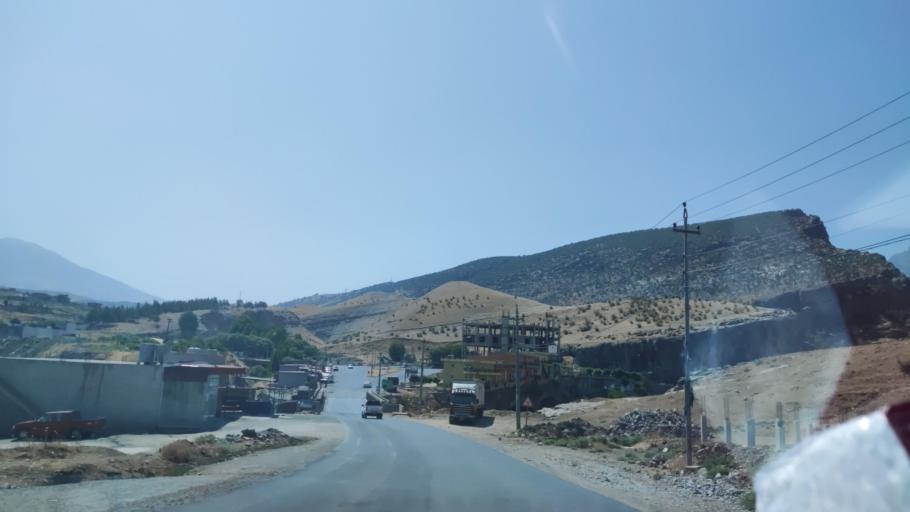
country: IQ
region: Arbil
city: Ruwandiz
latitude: 36.6504
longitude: 44.4980
